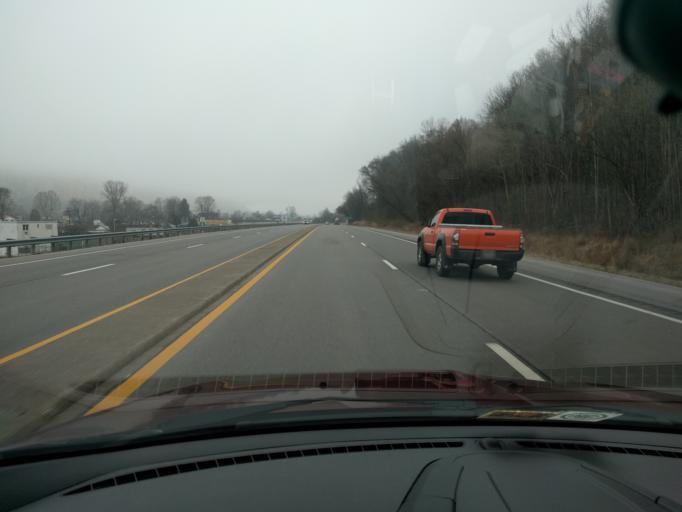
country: US
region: West Virginia
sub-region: Kanawha County
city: Rand
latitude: 38.2758
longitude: -81.5639
